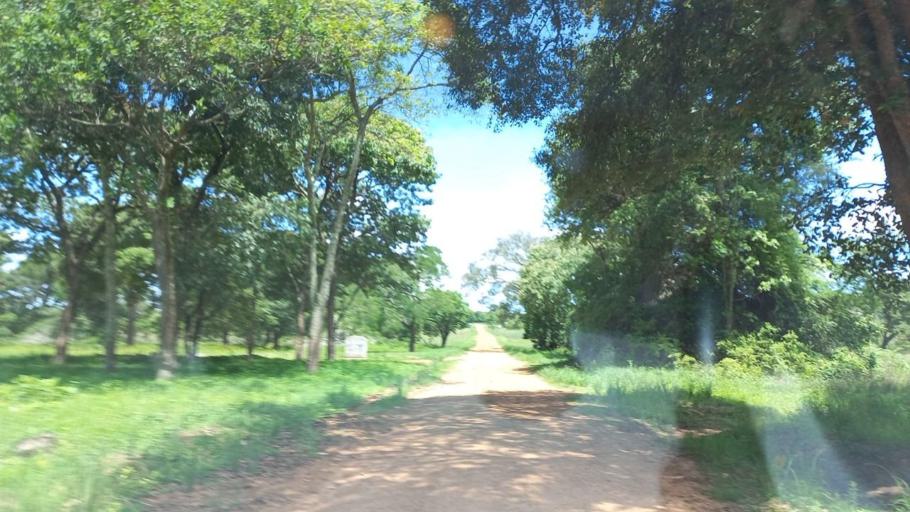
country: ZM
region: North-Western
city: Kabompo
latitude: -12.7512
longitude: 24.2682
